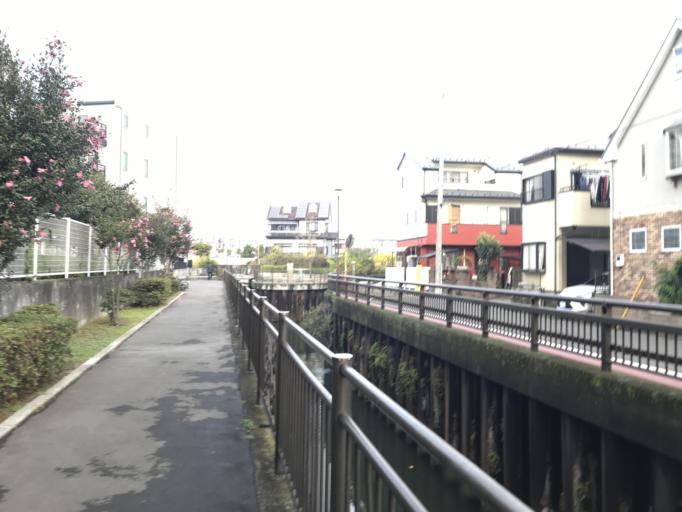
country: JP
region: Chiba
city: Funabashi
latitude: 35.7120
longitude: 139.9843
